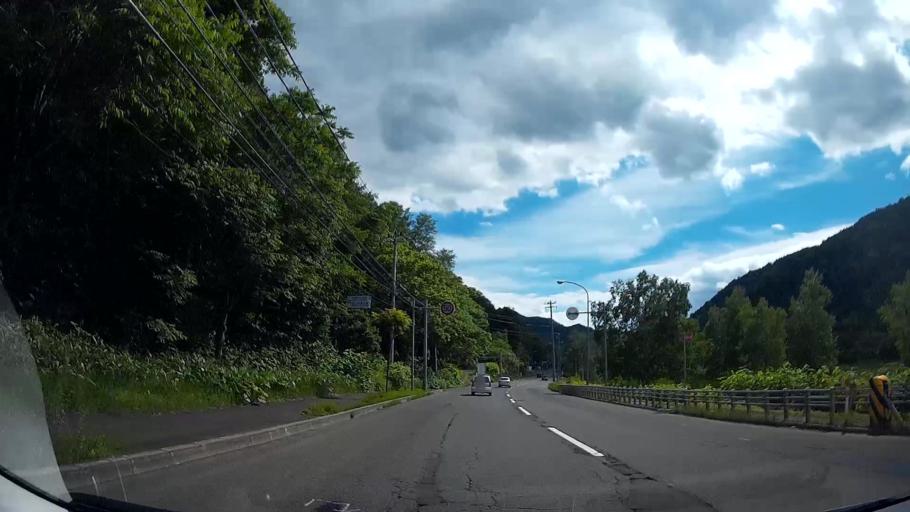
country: JP
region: Hokkaido
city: Sapporo
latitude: 42.9588
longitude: 141.1563
